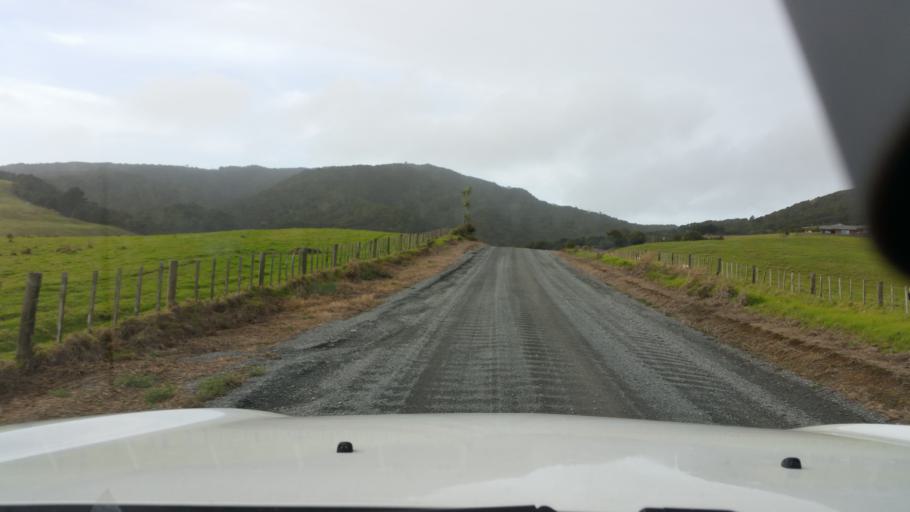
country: NZ
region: Northland
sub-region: Whangarei
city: Ngunguru
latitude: -35.7660
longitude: 174.5276
